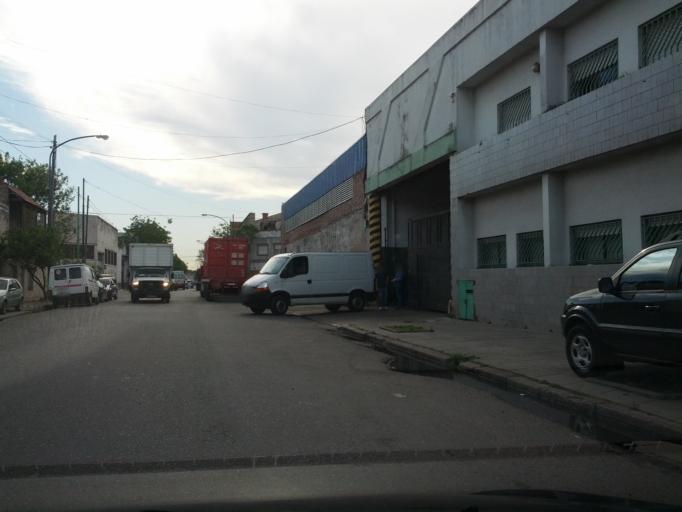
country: AR
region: Buenos Aires
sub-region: Partido de Avellaneda
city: Avellaneda
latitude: -34.6477
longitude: -58.4040
